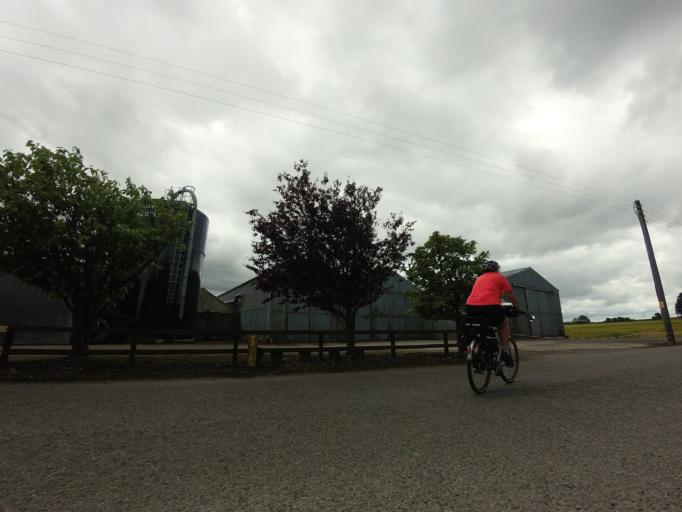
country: GB
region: Scotland
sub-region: Moray
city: Forres
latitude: 57.6101
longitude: -3.6864
